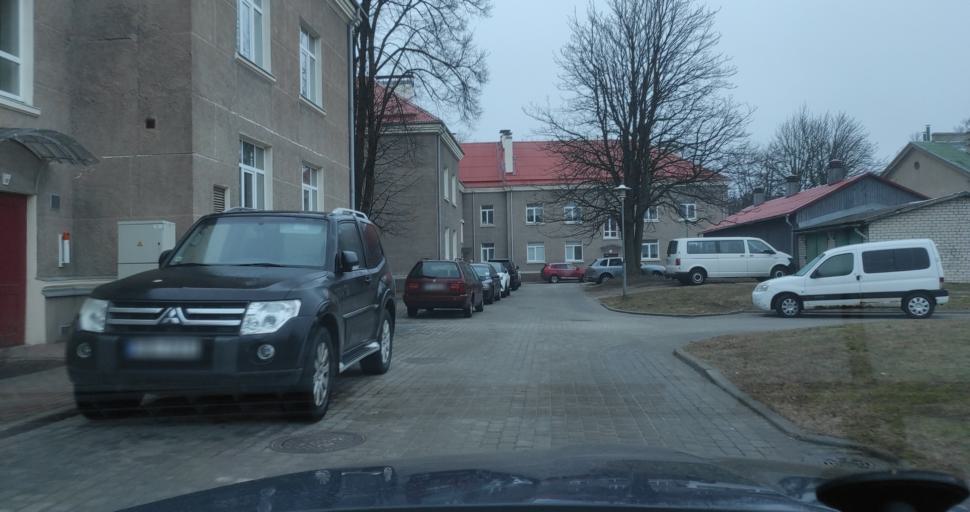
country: LV
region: Ventspils
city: Ventspils
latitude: 57.3888
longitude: 21.5499
